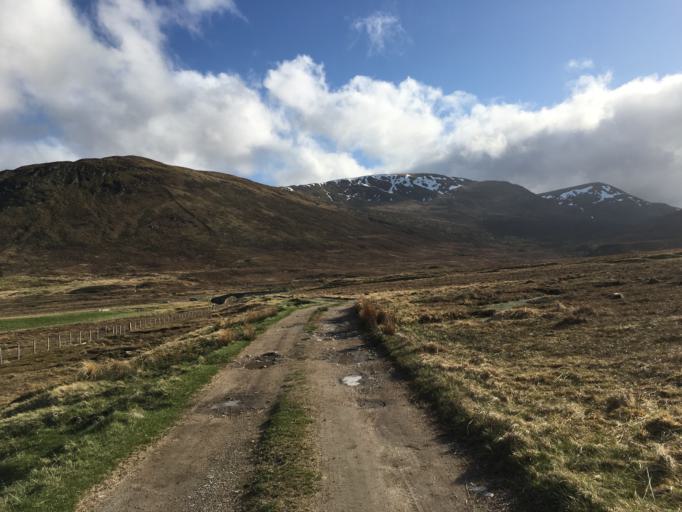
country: GB
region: Scotland
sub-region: Highland
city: Kingussie
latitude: 57.0233
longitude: -4.4344
